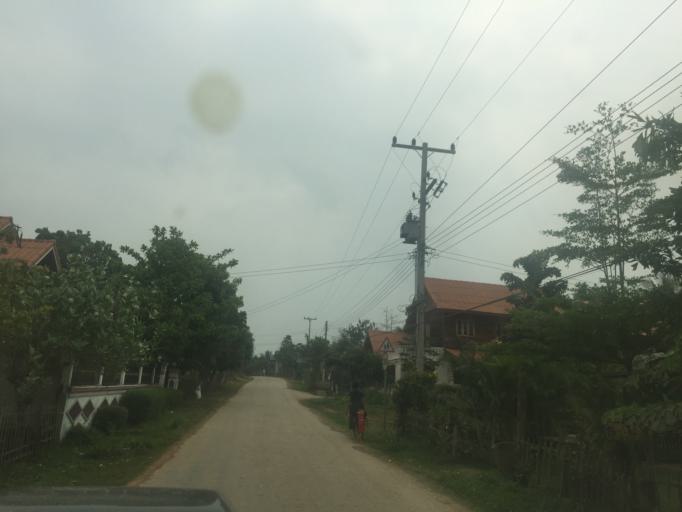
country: LA
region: Vientiane
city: Muang Sanakham
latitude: 18.3861
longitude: 101.5326
